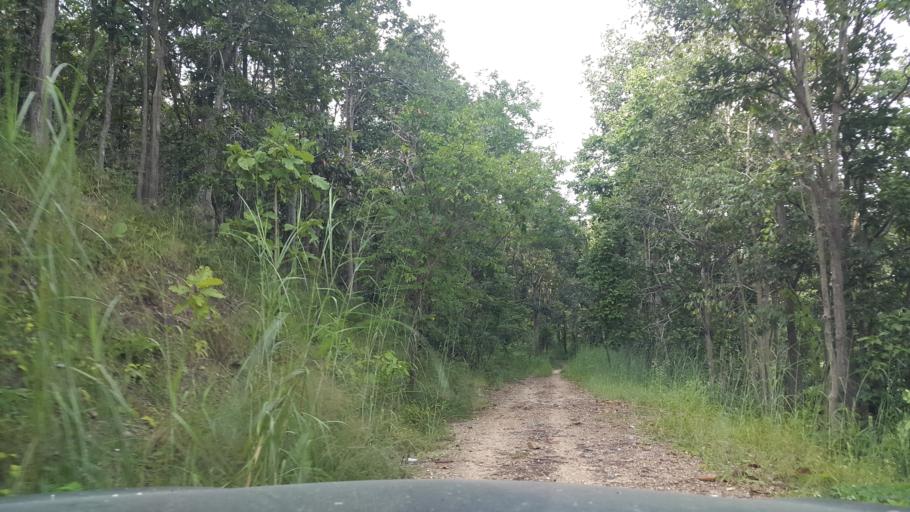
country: TH
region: Chiang Mai
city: San Sai
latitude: 18.9280
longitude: 99.0819
